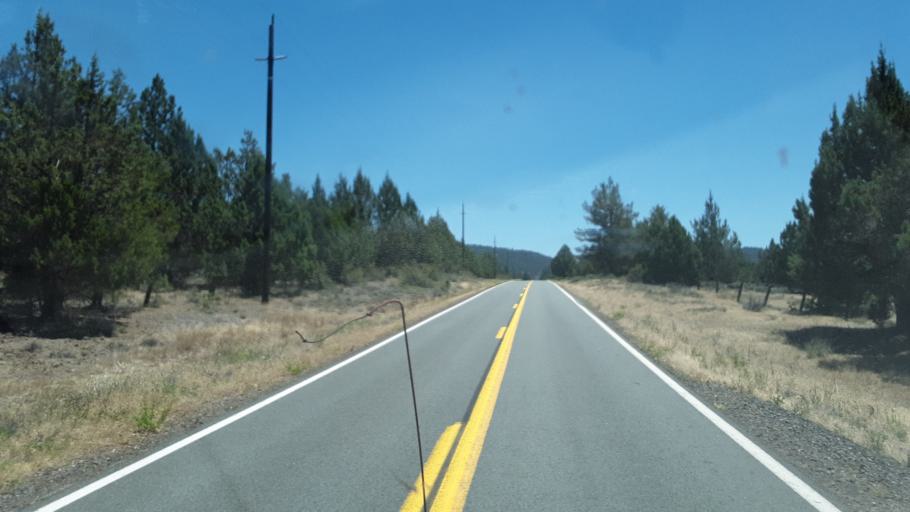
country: US
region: California
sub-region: Modoc County
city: Alturas
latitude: 41.0599
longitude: -120.8772
